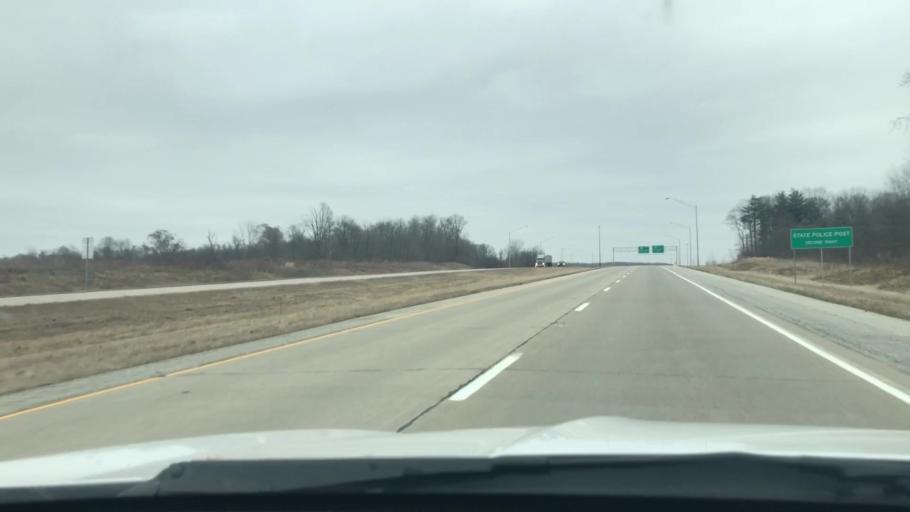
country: US
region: Indiana
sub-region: Miami County
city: Peru
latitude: 40.7710
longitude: -86.1403
